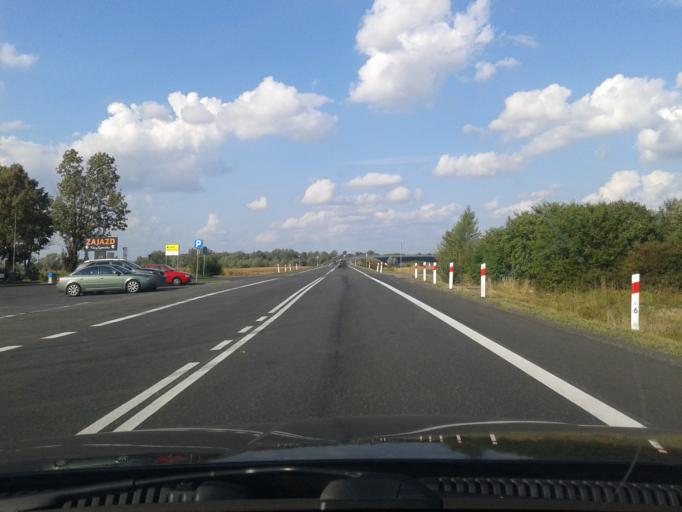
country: PL
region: Silesian Voivodeship
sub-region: Powiat wodzislawski
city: Olza
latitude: 49.9479
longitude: 18.3273
